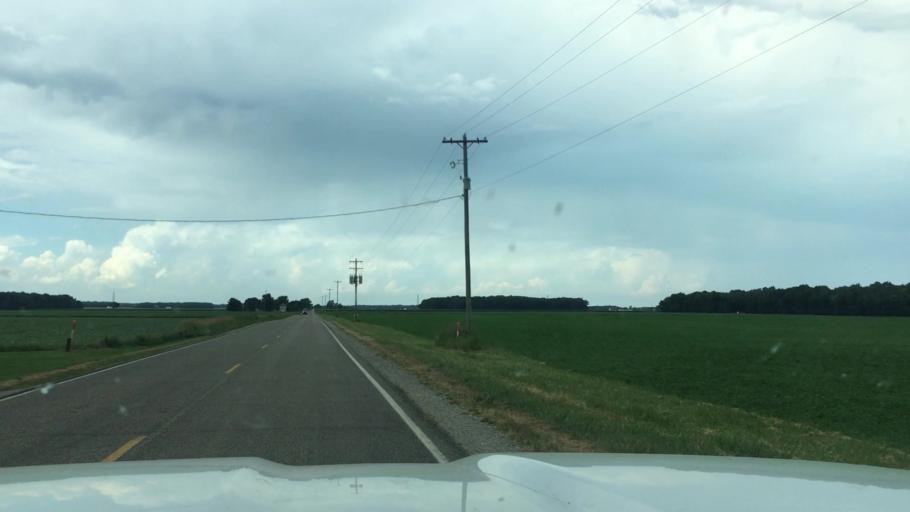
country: US
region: Michigan
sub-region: Montcalm County
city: Carson City
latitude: 43.1926
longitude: -84.7779
